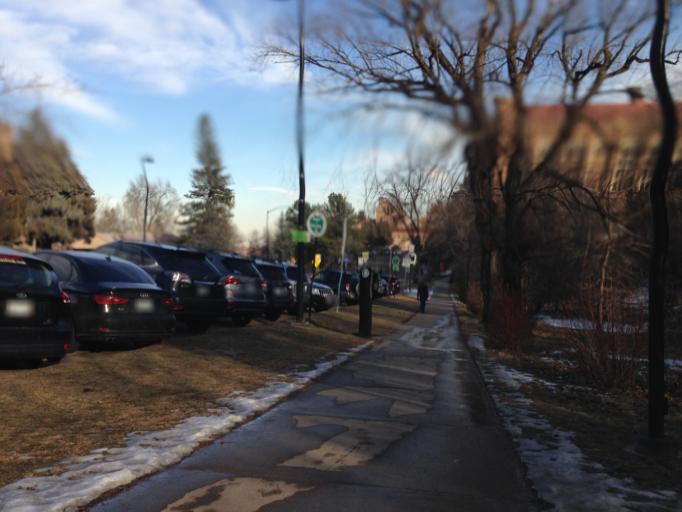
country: US
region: Colorado
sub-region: Boulder County
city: Boulder
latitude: 40.0104
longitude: -105.2747
